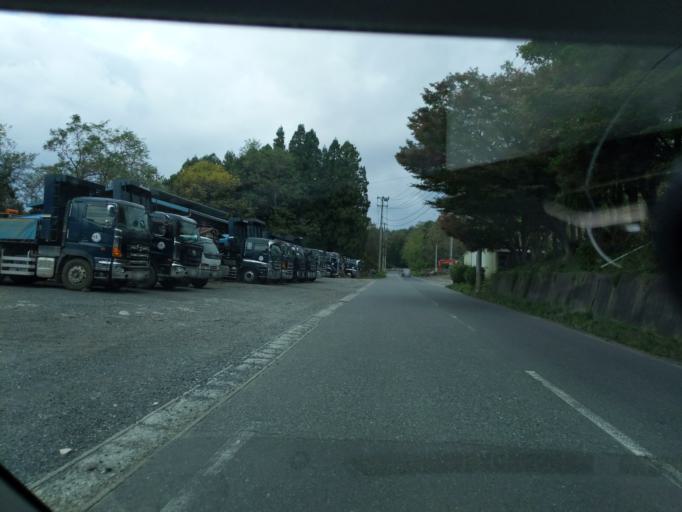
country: JP
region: Iwate
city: Mizusawa
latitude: 39.0484
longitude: 141.1137
